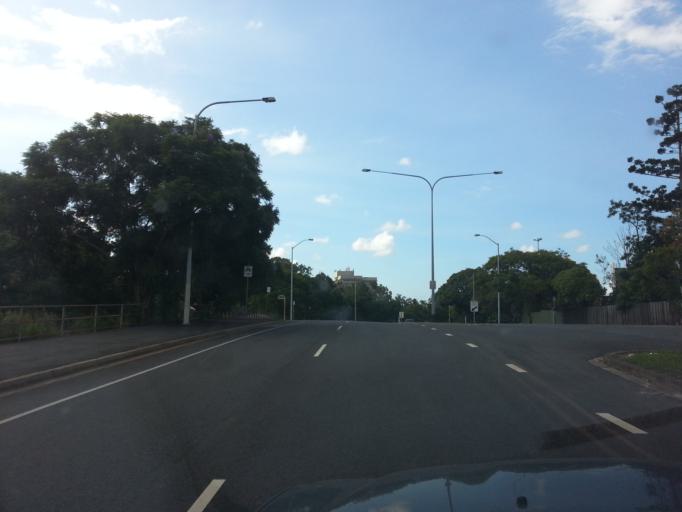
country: AU
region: Queensland
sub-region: Brisbane
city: Fortitude Valley
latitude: -27.4549
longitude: 153.0266
